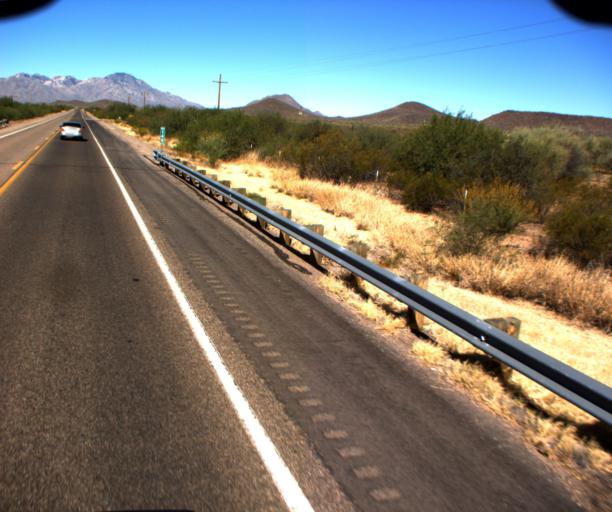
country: US
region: Arizona
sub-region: Pima County
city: Three Points
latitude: 32.0724
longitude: -111.3533
